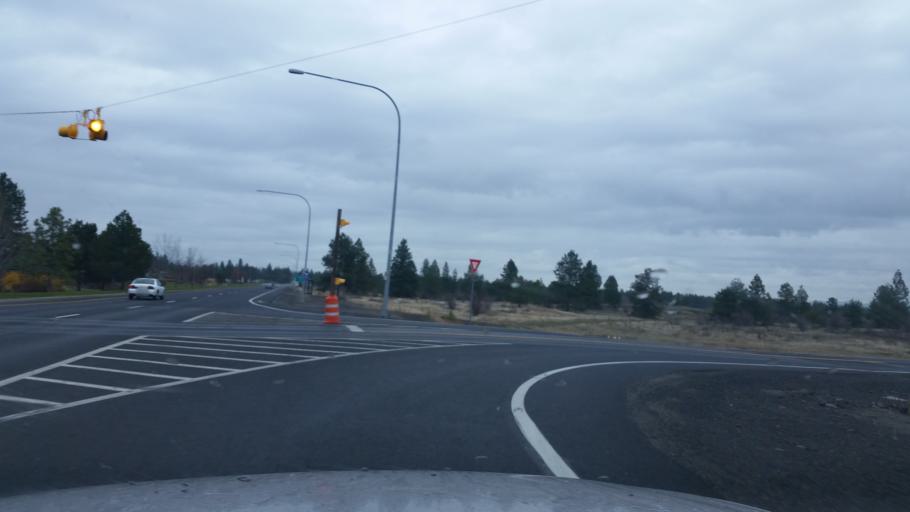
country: US
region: Washington
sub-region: Spokane County
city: Airway Heights
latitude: 47.6354
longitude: -117.5177
